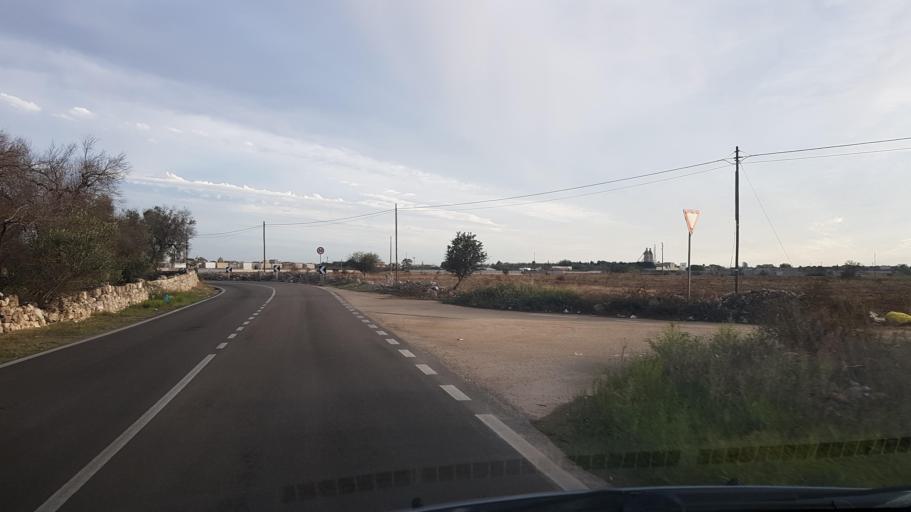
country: IT
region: Apulia
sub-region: Provincia di Lecce
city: Surbo
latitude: 40.4079
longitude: 18.1258
